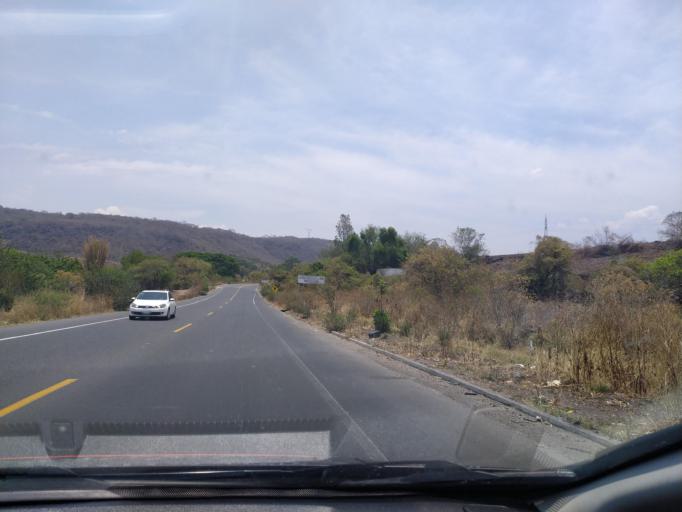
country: MX
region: Jalisco
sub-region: Acatlan de Juarez
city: Villa de los Ninos
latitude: 20.4154
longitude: -103.5859
